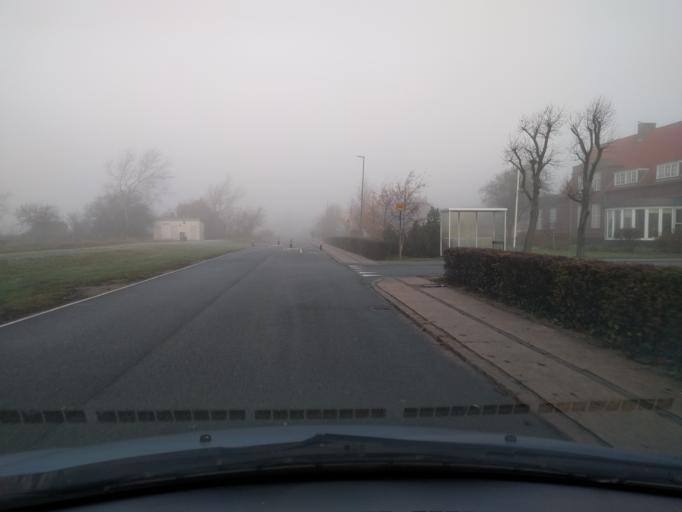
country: DK
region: South Denmark
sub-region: Kerteminde Kommune
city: Kerteminde
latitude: 55.4501
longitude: 10.6501
